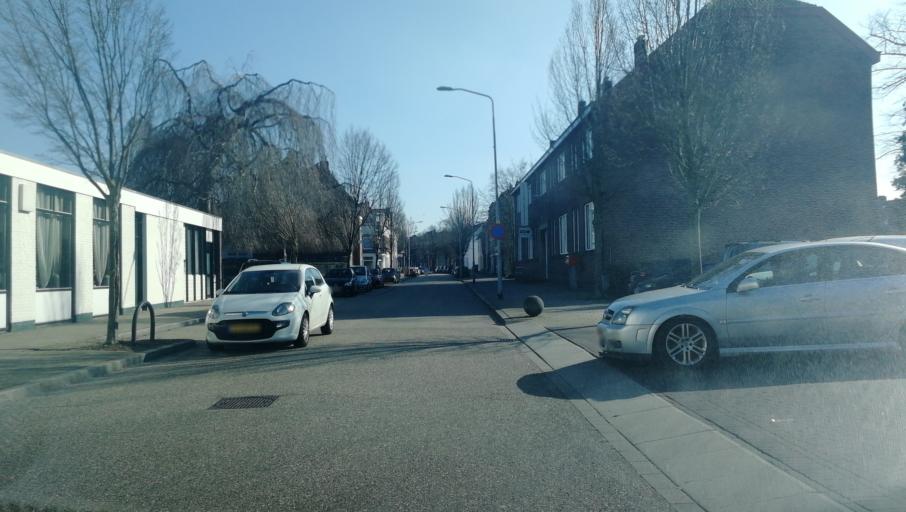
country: NL
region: Limburg
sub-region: Gemeente Venlo
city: Venlo
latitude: 51.3596
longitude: 6.1804
